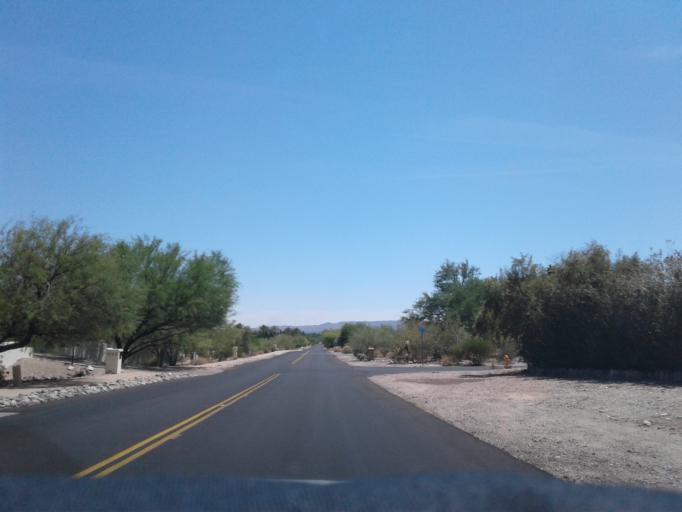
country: US
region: Arizona
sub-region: Maricopa County
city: Paradise Valley
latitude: 33.5273
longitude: -112.0040
